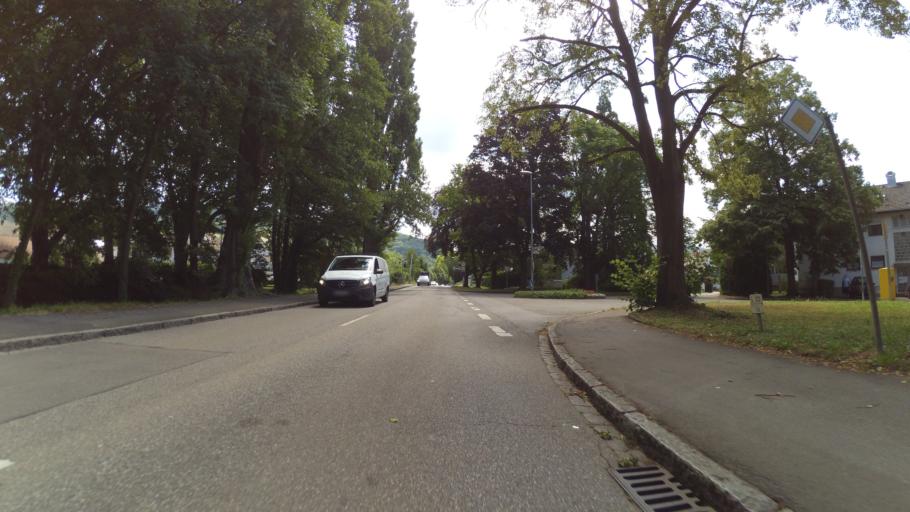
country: DE
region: Baden-Wuerttemberg
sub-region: Freiburg Region
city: Bad Krozingen
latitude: 47.8836
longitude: 7.7276
